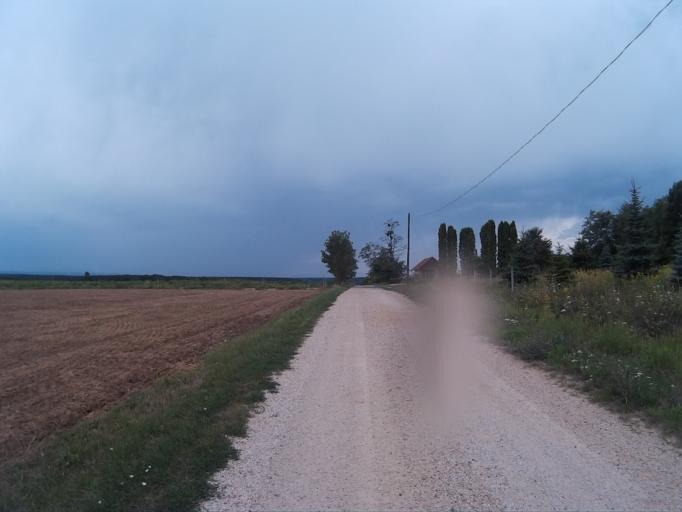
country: SI
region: Kobilje
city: Kobilje
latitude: 46.7508
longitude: 16.4533
